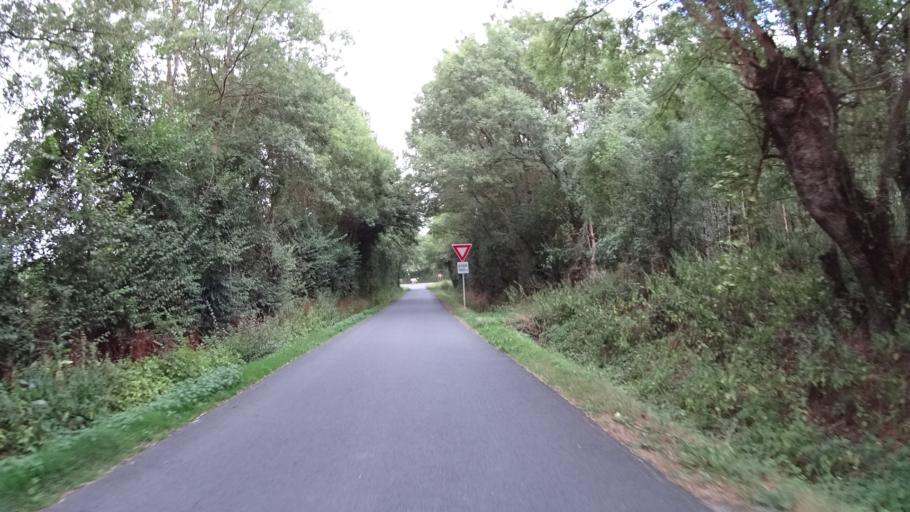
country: FR
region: Pays de la Loire
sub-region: Departement de la Loire-Atlantique
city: Saint-Gereon
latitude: 47.3608
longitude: -1.2042
